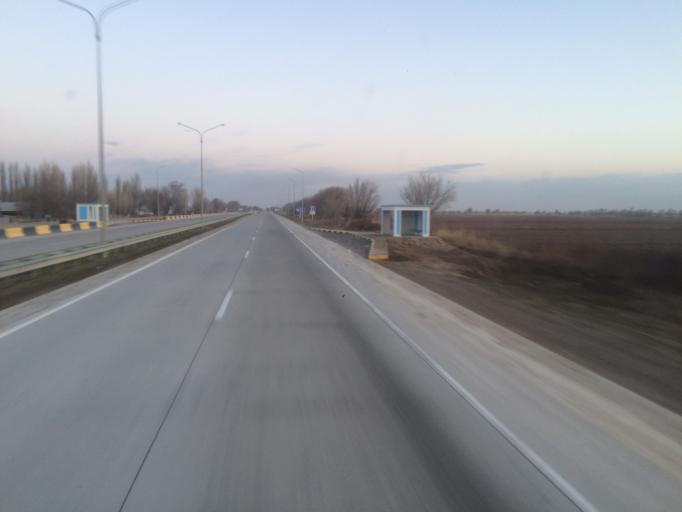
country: KZ
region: Ongtustik Qazaqstan
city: Shayan
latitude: 42.9594
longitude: 68.8900
